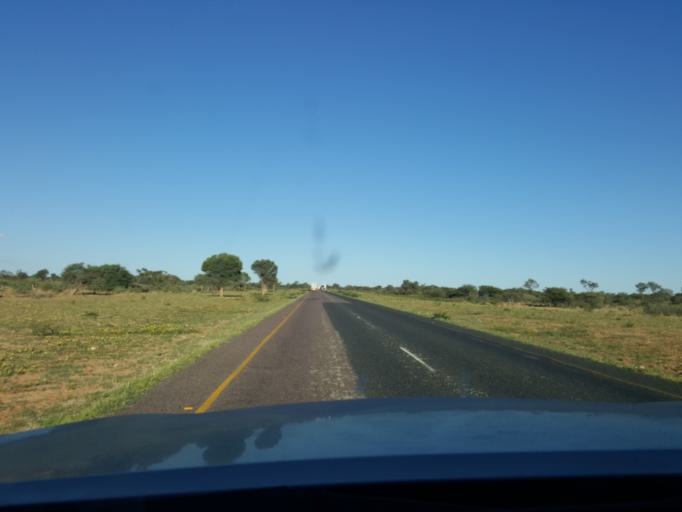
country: BW
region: Southern
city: Khakhea
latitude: -24.2597
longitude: 23.3123
